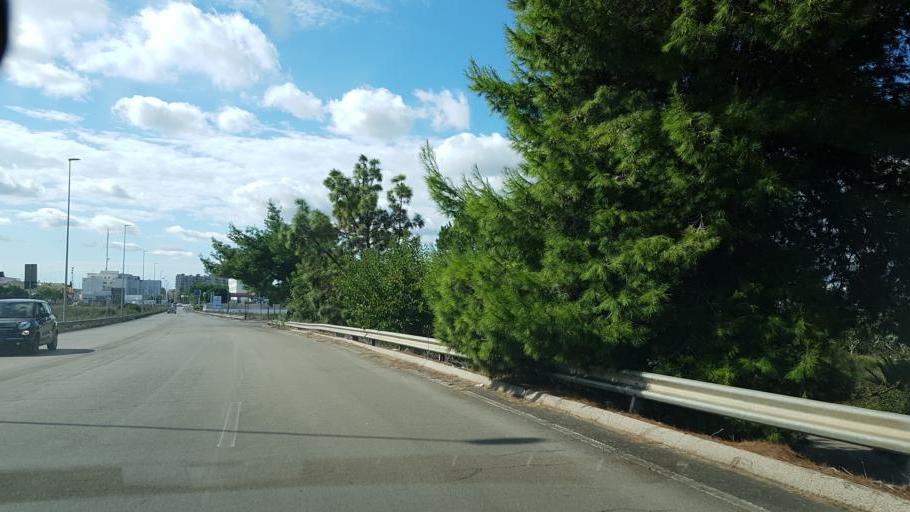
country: IT
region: Apulia
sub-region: Provincia di Lecce
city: Lecce
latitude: 40.3651
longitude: 18.1595
